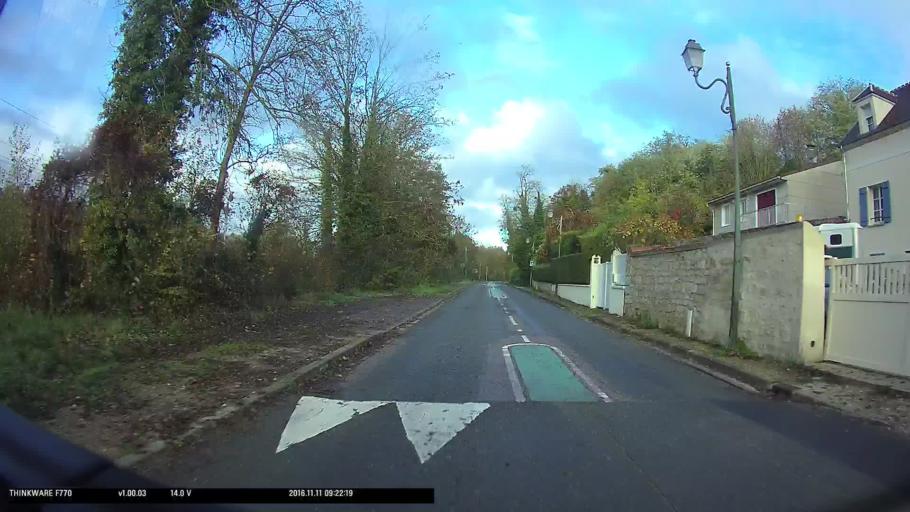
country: FR
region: Ile-de-France
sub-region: Departement du Val-d'Oise
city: Ableiges
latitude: 49.0815
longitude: 2.0021
